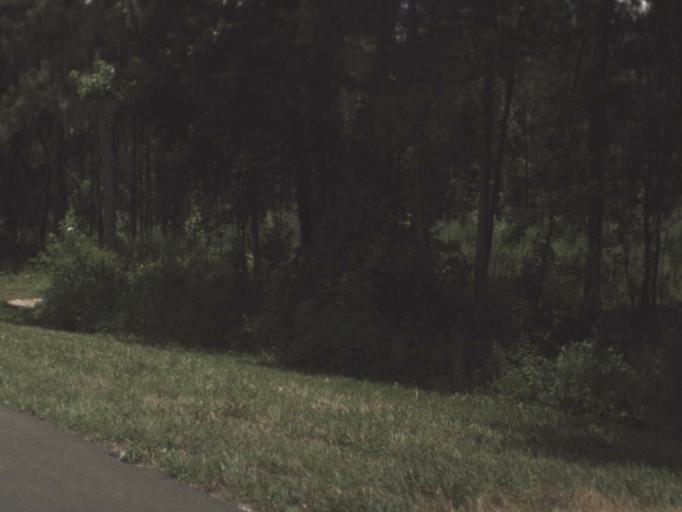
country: US
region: Florida
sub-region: Alachua County
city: Alachua
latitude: 29.7836
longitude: -82.3762
